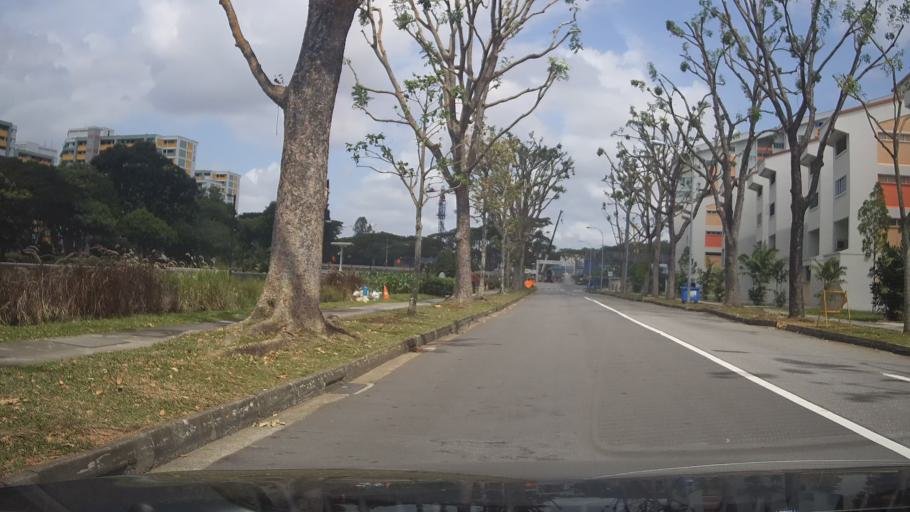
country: SG
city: Singapore
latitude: 1.3343
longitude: 103.8651
